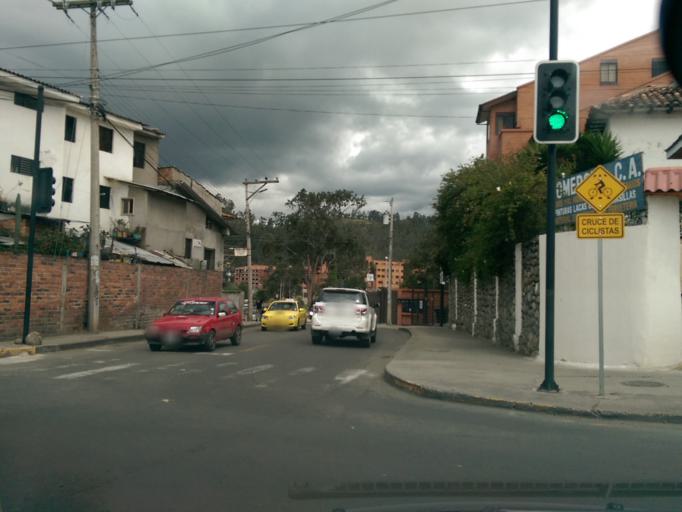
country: EC
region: Azuay
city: Cuenca
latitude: -2.9096
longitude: -79.0134
